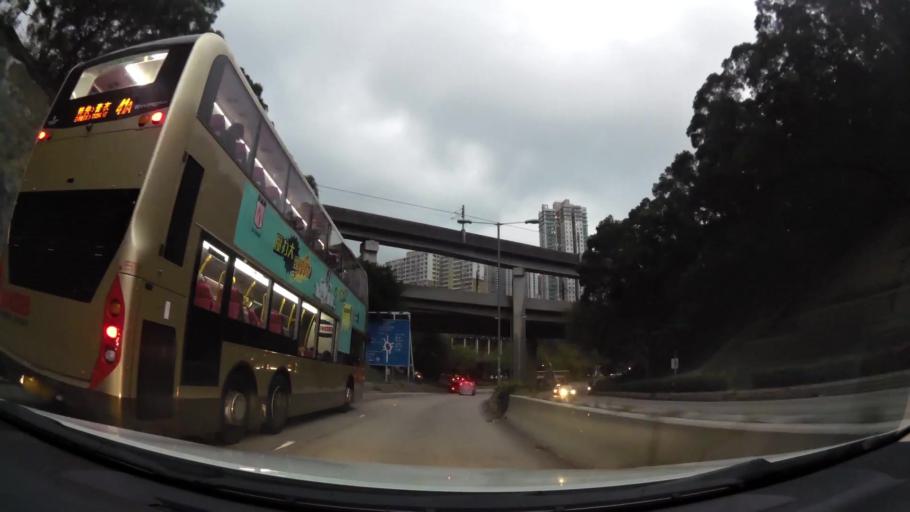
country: HK
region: Tsuen Wan
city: Tsuen Wan
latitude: 22.3586
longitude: 114.1018
